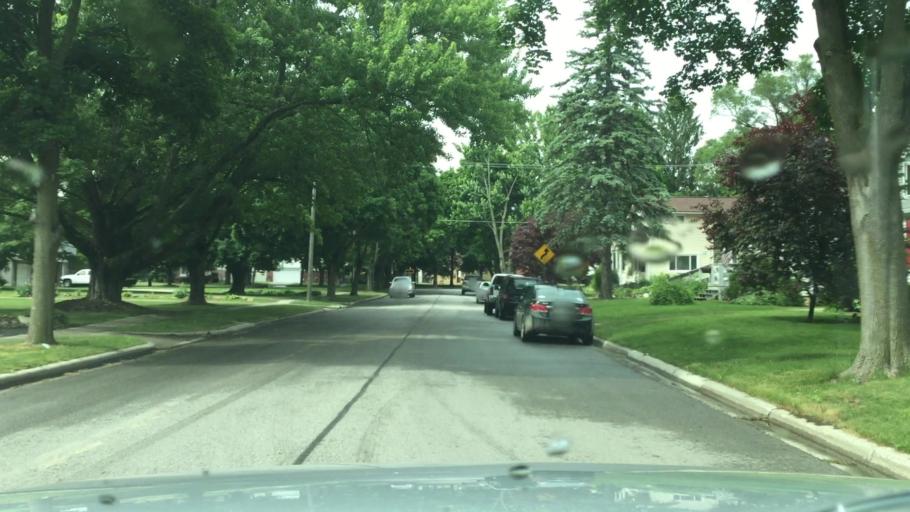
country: US
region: Michigan
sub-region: Lapeer County
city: Lapeer
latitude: 43.0531
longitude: -83.3257
